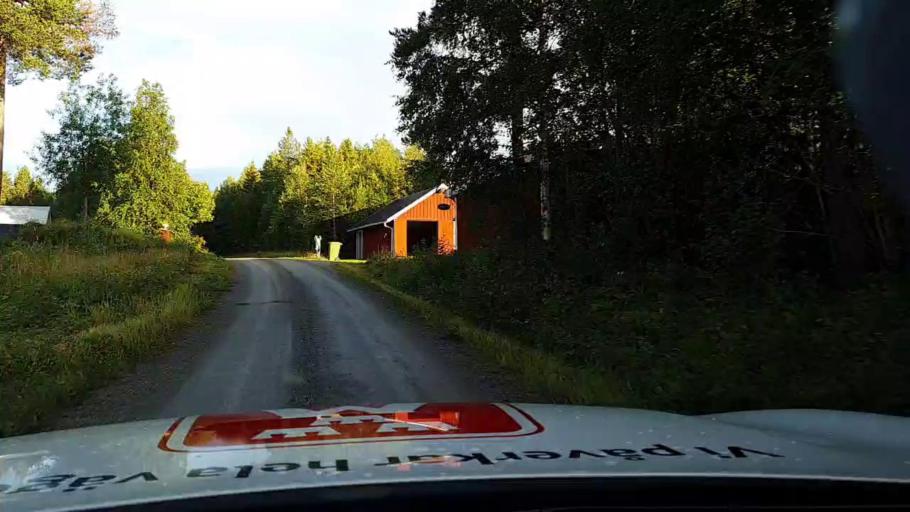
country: SE
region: Jaemtland
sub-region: Bergs Kommun
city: Hoverberg
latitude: 62.8530
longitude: 14.5375
